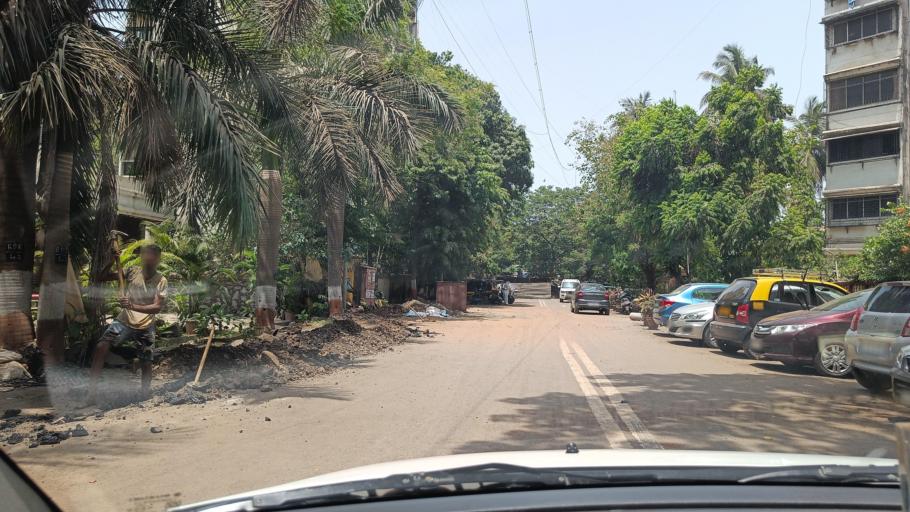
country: IN
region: Maharashtra
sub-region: Mumbai Suburban
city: Mumbai
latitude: 19.0522
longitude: 72.8770
